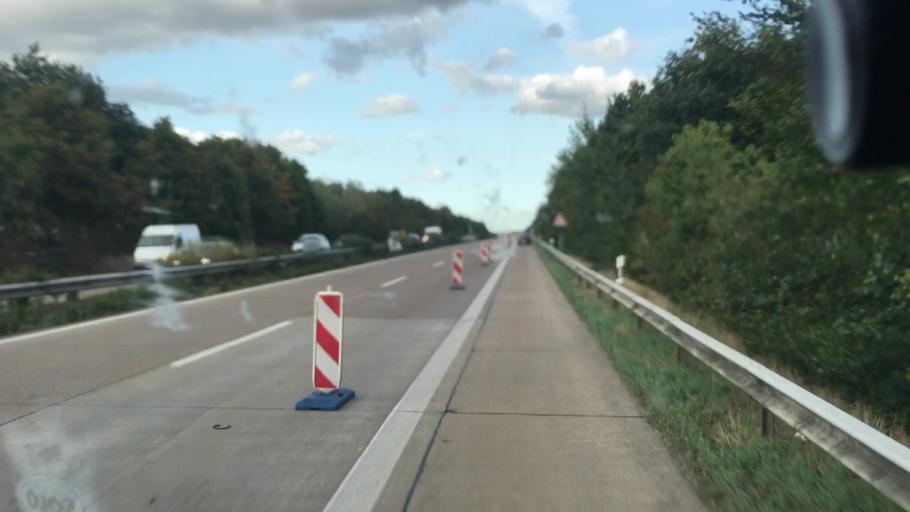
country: DE
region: Lower Saxony
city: Wardenburg
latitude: 53.0721
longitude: 8.2436
